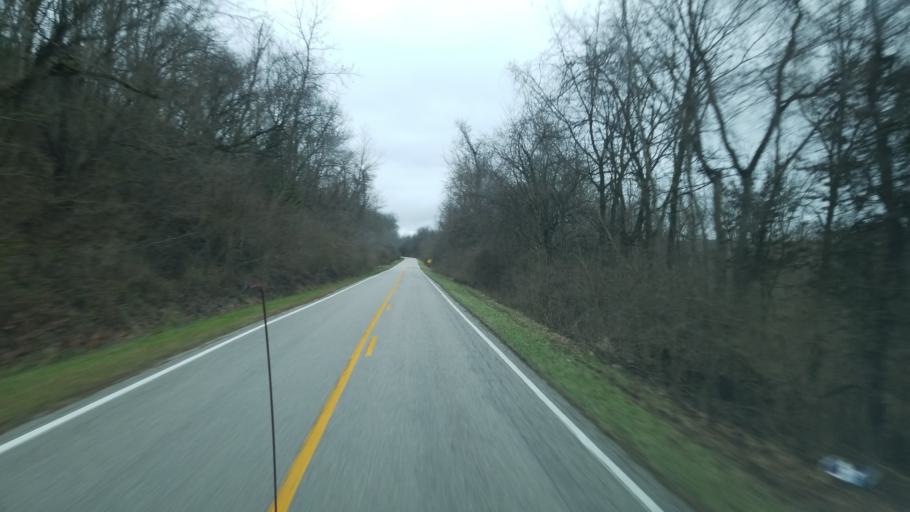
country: US
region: Kentucky
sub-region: Bracken County
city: Brooksville
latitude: 38.7742
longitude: -84.1217
